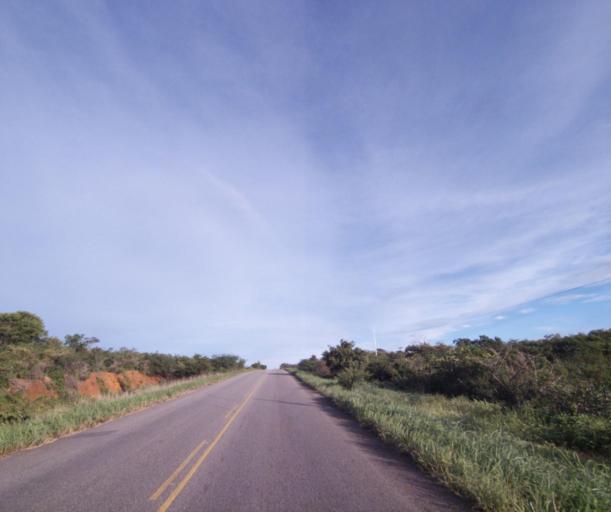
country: BR
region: Bahia
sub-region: Caetite
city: Caetite
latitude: -14.1768
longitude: -42.1767
